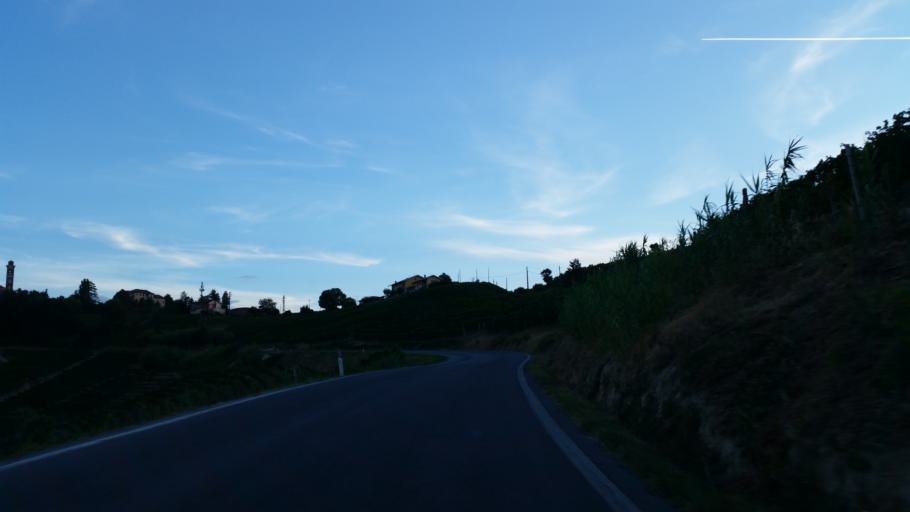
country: IT
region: Piedmont
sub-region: Provincia di Cuneo
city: Castiglione Tinella
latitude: 44.7316
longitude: 8.1928
